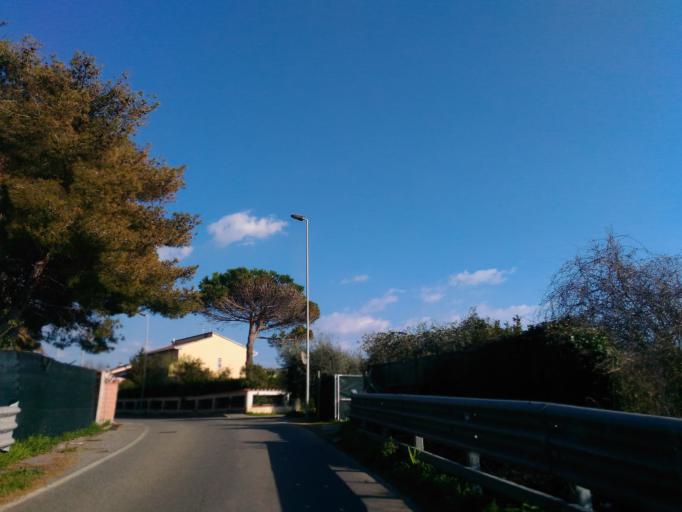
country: IT
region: Tuscany
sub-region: Provincia di Livorno
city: Livorno
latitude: 43.5116
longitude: 10.3343
